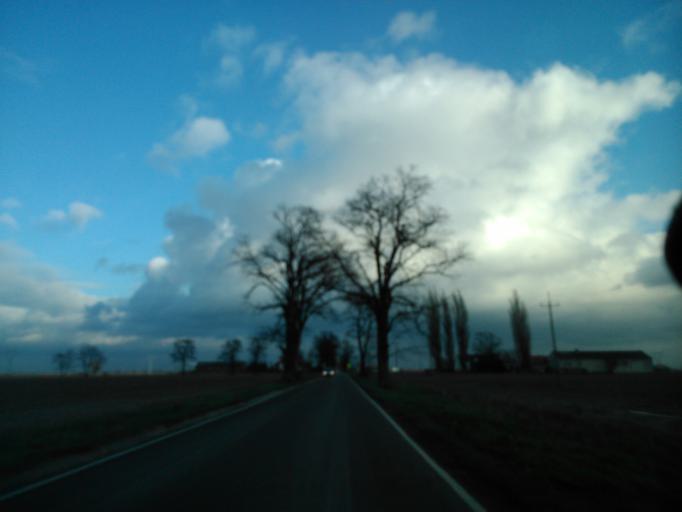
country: PL
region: Masovian Voivodeship
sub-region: Powiat warszawski zachodni
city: Leszno
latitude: 52.2432
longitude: 20.6180
